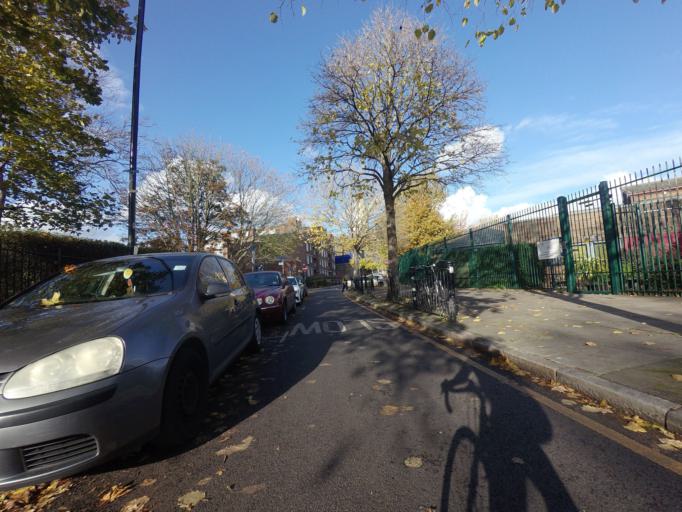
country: GB
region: England
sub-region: Greater London
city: Poplar
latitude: 51.5101
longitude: -0.0303
